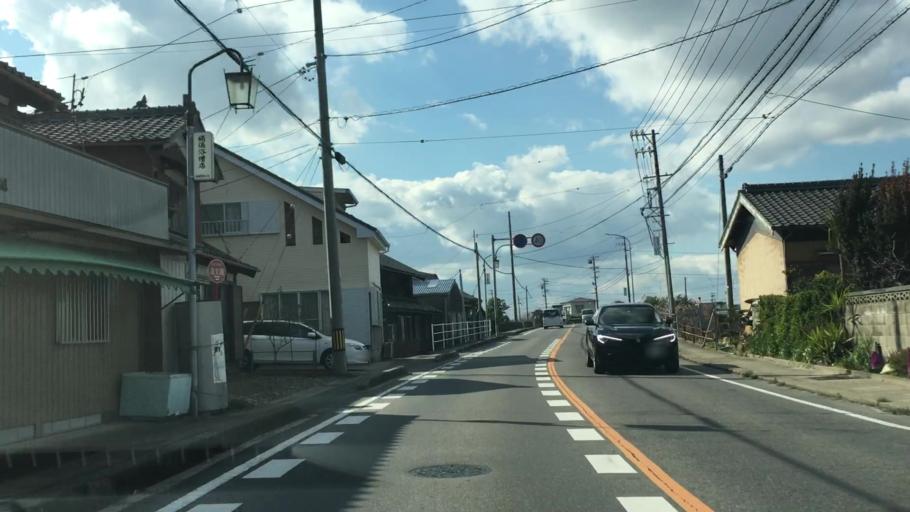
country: JP
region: Aichi
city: Ishiki
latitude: 34.7968
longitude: 137.0558
